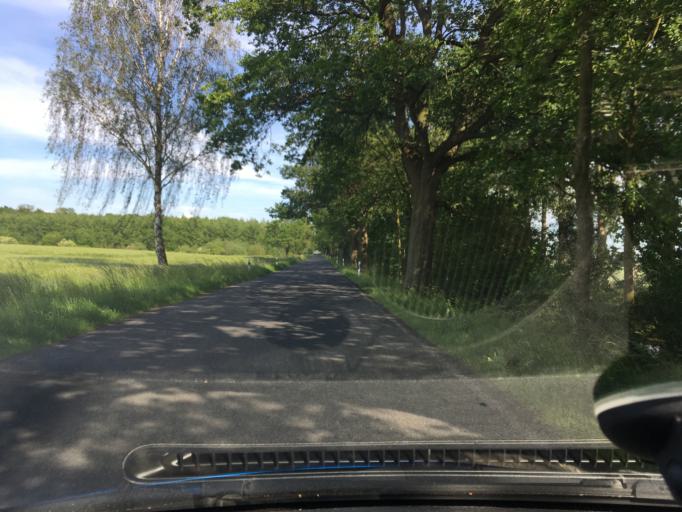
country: DE
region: Lower Saxony
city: Neu Darchau
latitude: 53.3325
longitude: 10.8697
